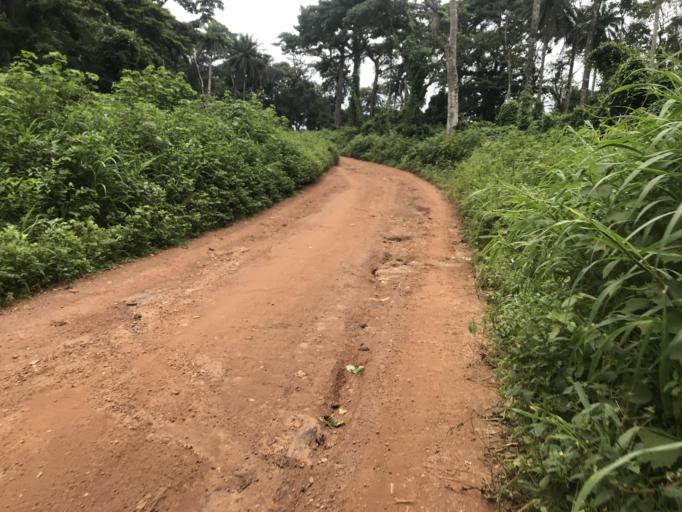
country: SL
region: Eastern Province
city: Buedu
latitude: 8.3953
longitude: -10.3991
